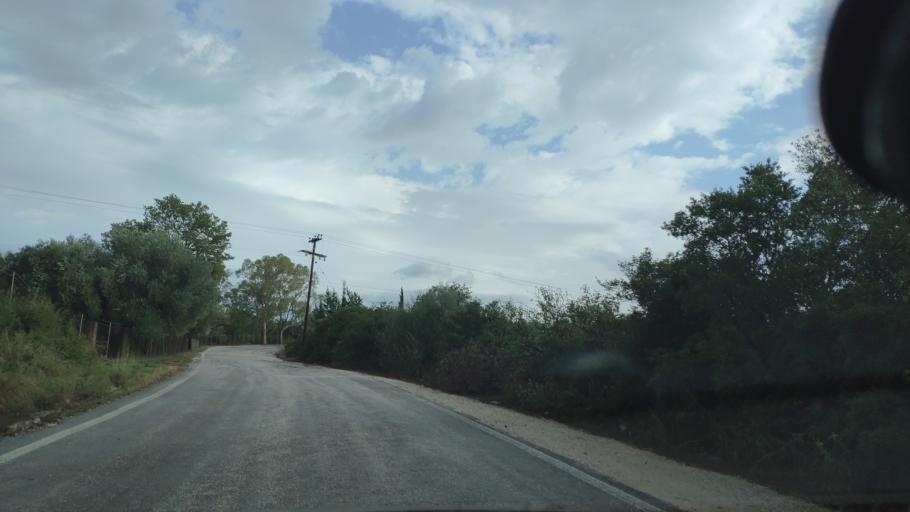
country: GR
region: West Greece
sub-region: Nomos Aitolias kai Akarnanias
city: Sardinia
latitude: 38.8881
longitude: 21.2179
